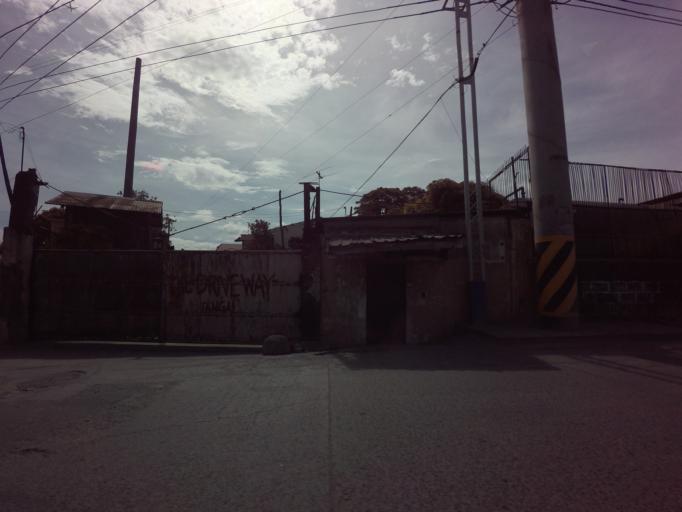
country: PH
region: Calabarzon
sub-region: Province of Rizal
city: Pateros
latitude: 14.5440
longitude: 121.0886
